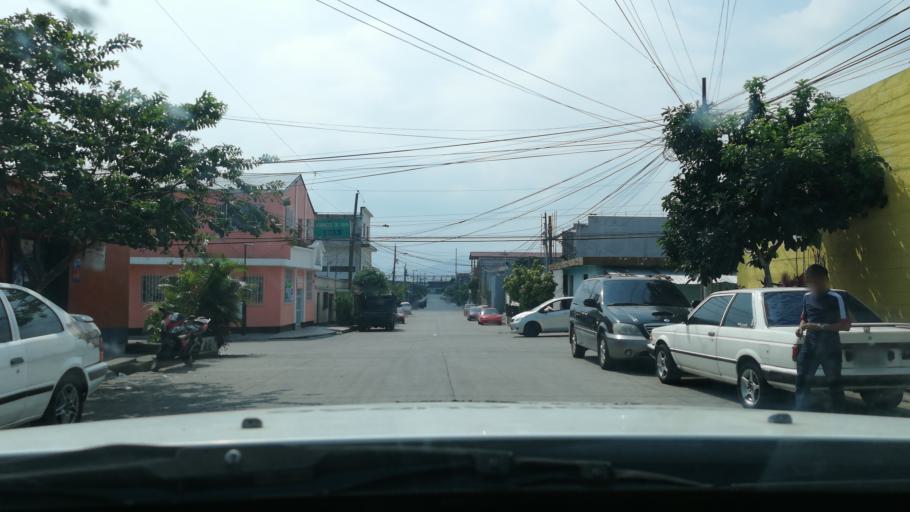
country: GT
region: Guatemala
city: Petapa
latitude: 14.5080
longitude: -90.5664
